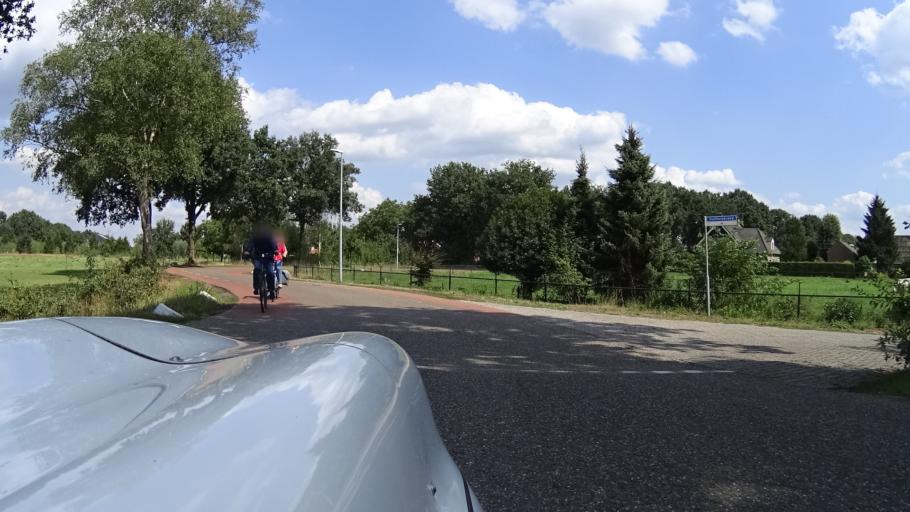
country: NL
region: North Brabant
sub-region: Gemeente Veghel
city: Mariaheide
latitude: 51.6420
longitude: 5.5884
